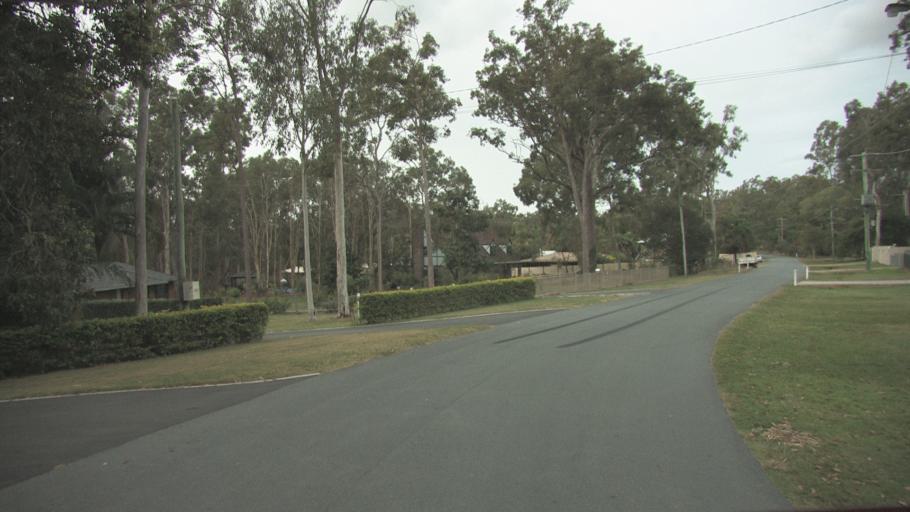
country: AU
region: Queensland
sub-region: Logan
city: Park Ridge South
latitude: -27.6824
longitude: 153.0143
